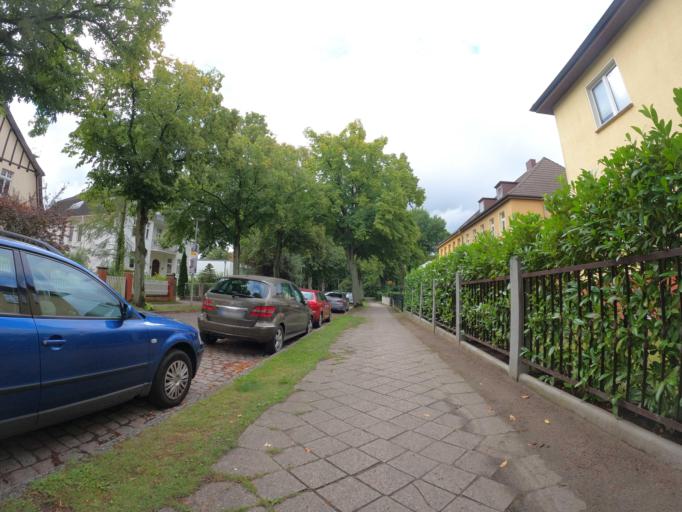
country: DE
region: Mecklenburg-Vorpommern
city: Stralsund
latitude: 54.3222
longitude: 13.0820
